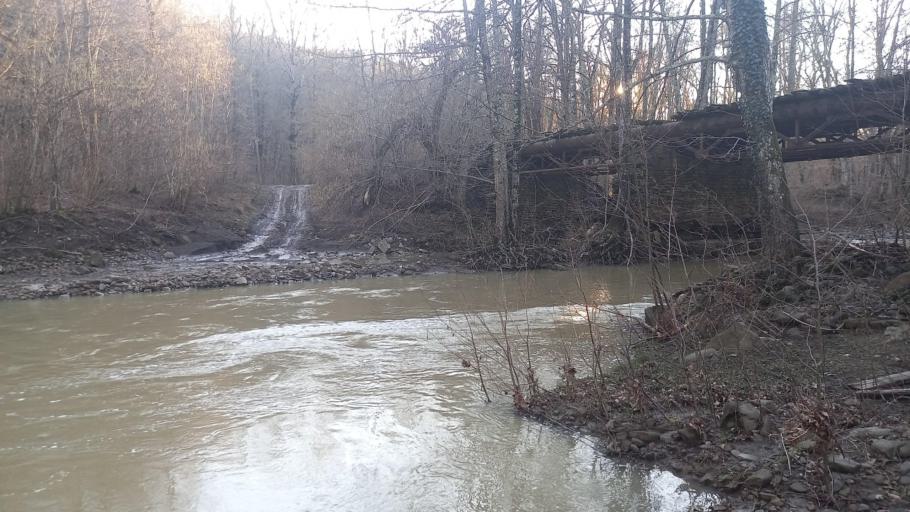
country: RU
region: Krasnodarskiy
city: Smolenskaya
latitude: 44.6109
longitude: 38.7404
